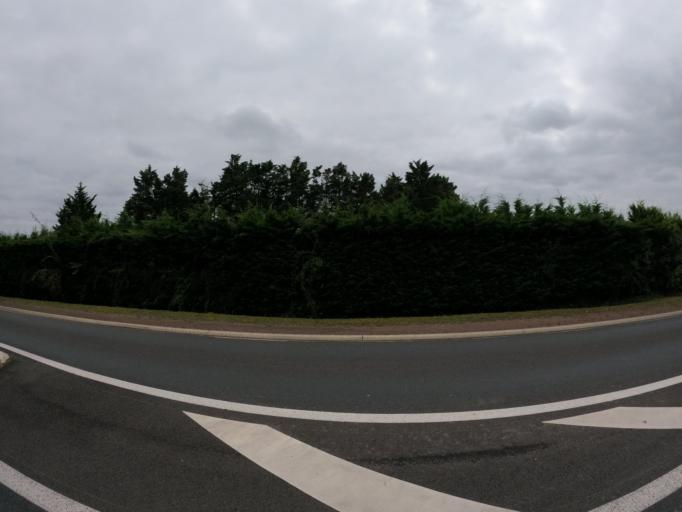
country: FR
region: Pays de la Loire
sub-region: Departement de la Vendee
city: Nalliers
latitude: 46.5253
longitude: -0.9959
